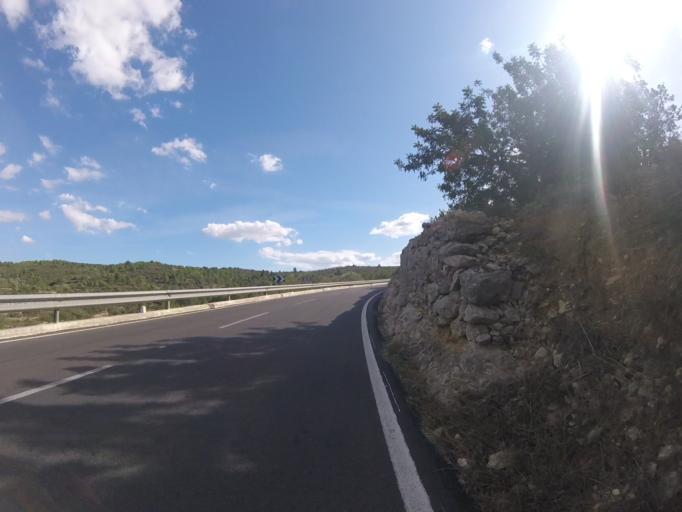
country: ES
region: Valencia
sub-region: Provincia de Castello
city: Cuevas de Vinroma
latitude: 40.3201
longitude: 0.1335
